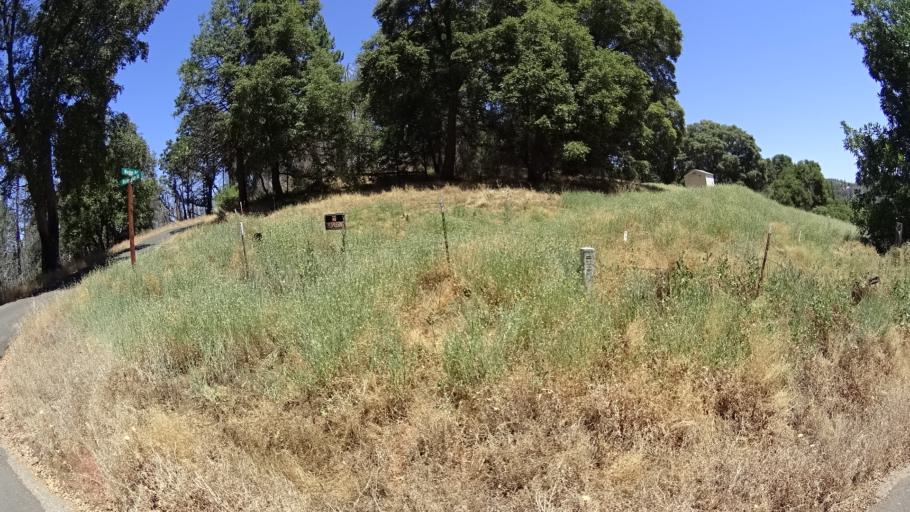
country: US
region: California
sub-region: Calaveras County
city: Mountain Ranch
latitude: 38.2735
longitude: -120.5905
